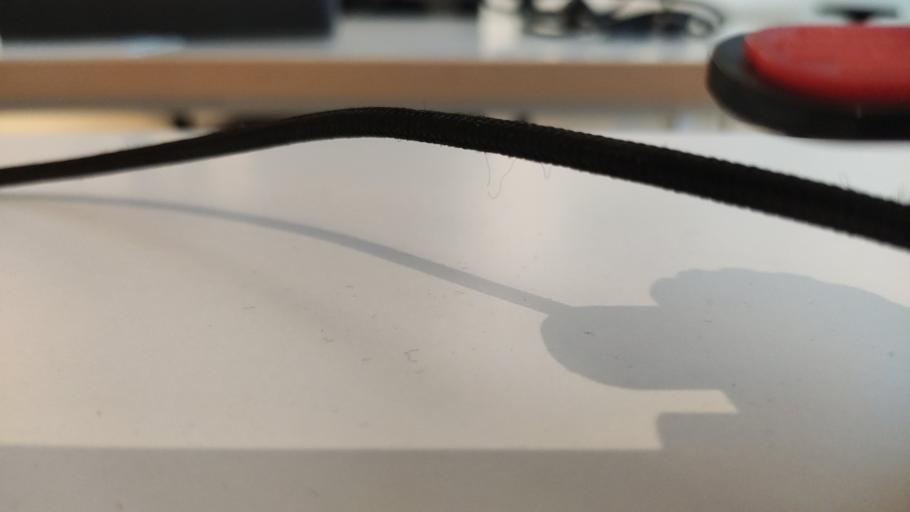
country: RU
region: Moskovskaya
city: Novopetrovskoye
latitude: 55.9063
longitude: 36.4424
